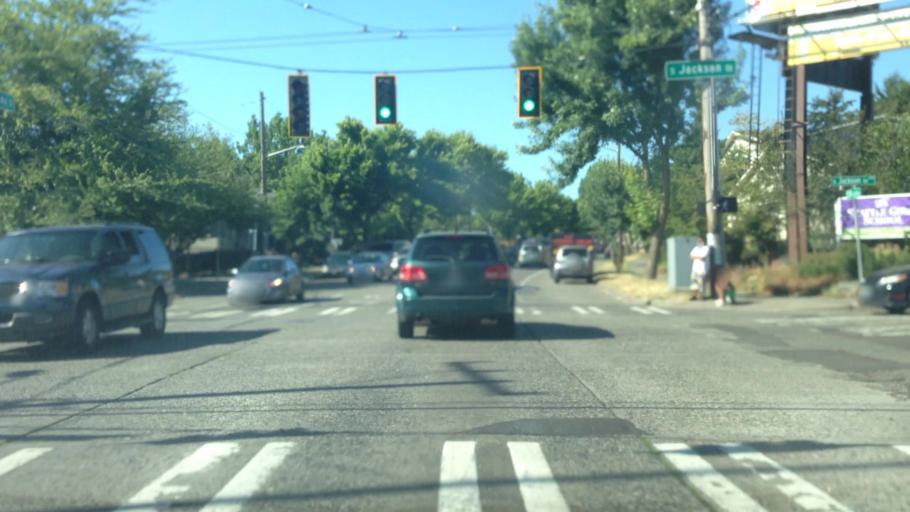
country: US
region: Washington
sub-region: King County
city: Seattle
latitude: 47.5991
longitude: -122.2974
